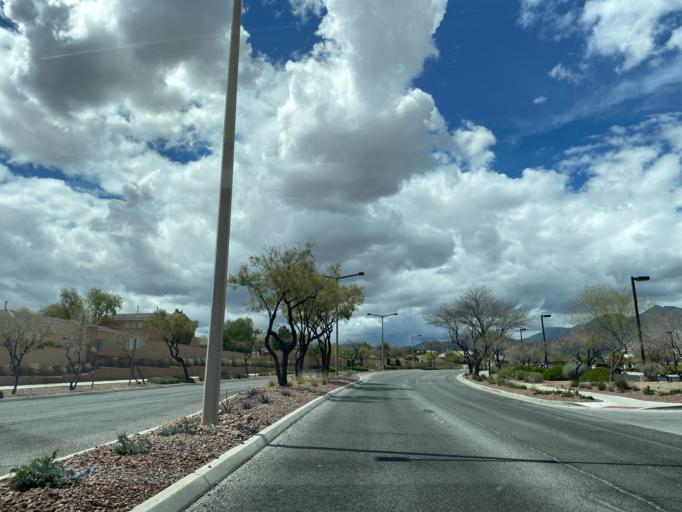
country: US
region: Nevada
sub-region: Clark County
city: Summerlin South
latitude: 36.1675
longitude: -115.3254
